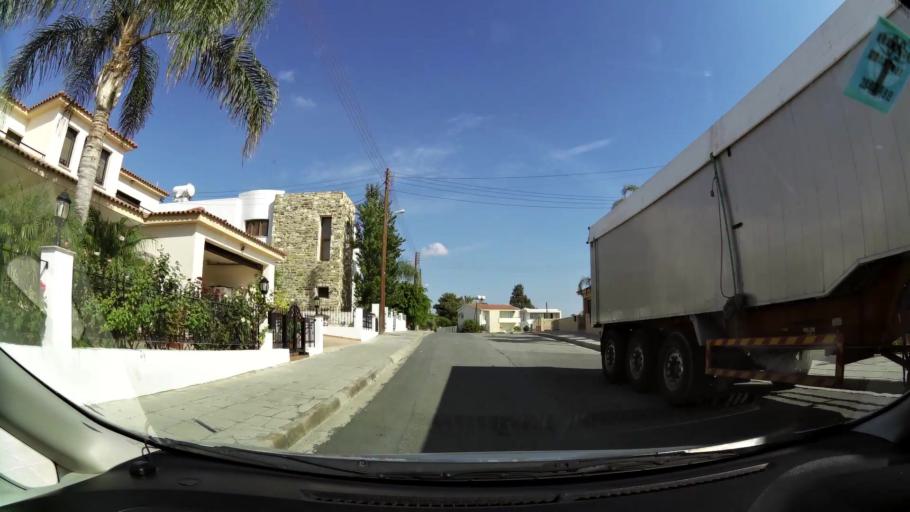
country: CY
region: Larnaka
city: Aradippou
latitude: 34.9495
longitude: 33.5797
